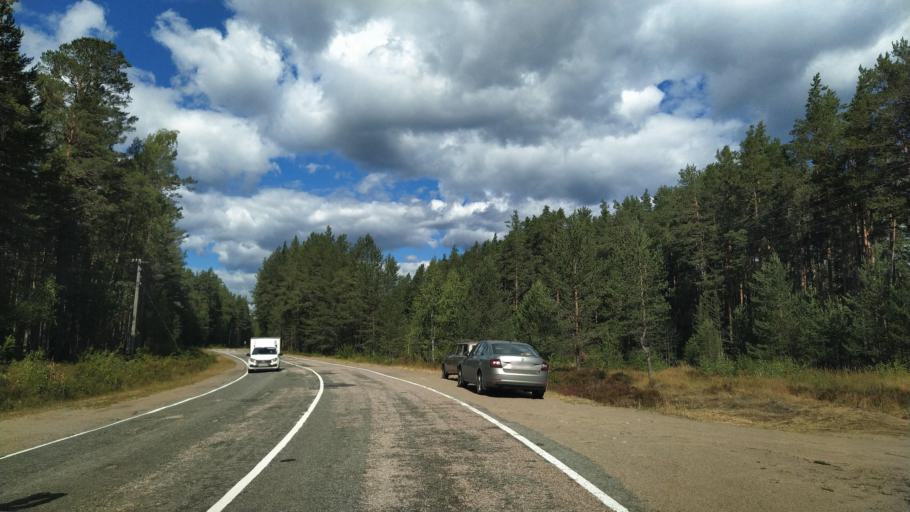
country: RU
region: Leningrad
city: Priozersk
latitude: 60.9951
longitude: 30.2543
